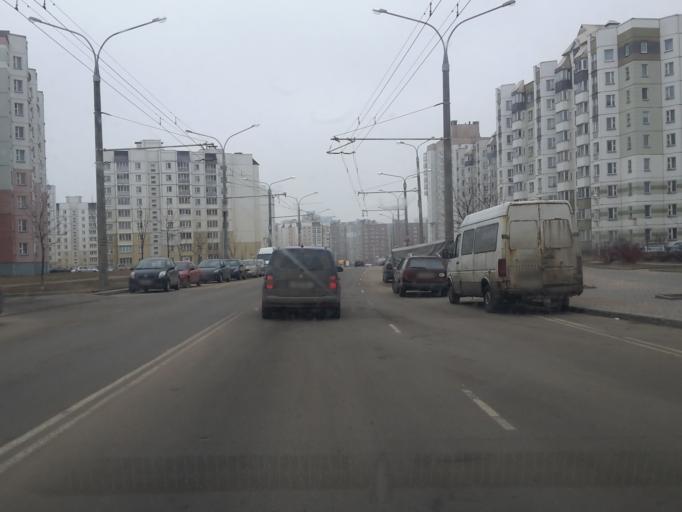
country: BY
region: Minsk
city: Novoye Medvezhino
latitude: 53.8916
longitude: 27.4214
